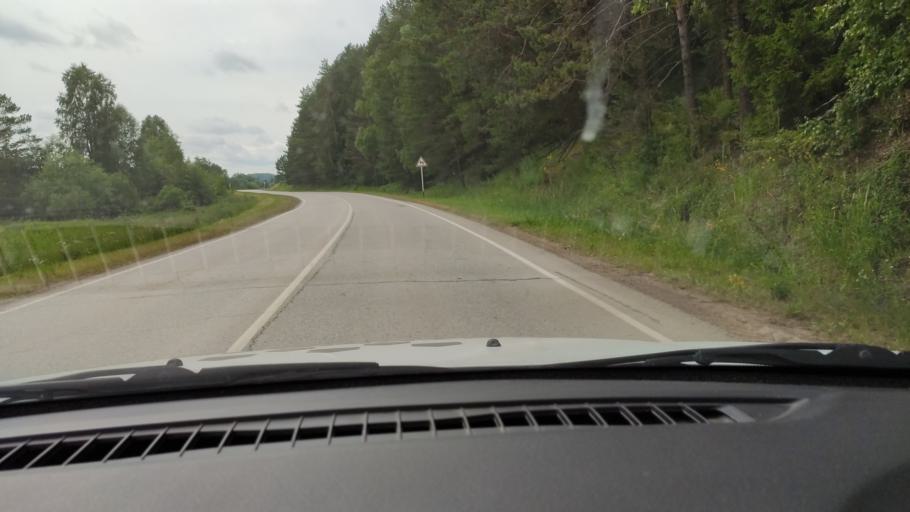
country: RU
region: Perm
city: Kukushtan
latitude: 57.4878
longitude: 56.6226
